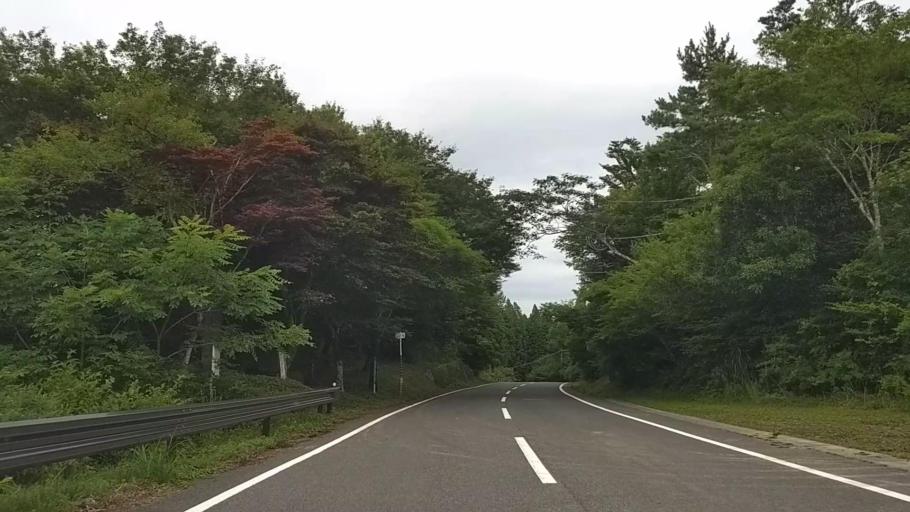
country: JP
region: Shizuoka
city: Gotemba
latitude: 35.3208
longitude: 139.0106
